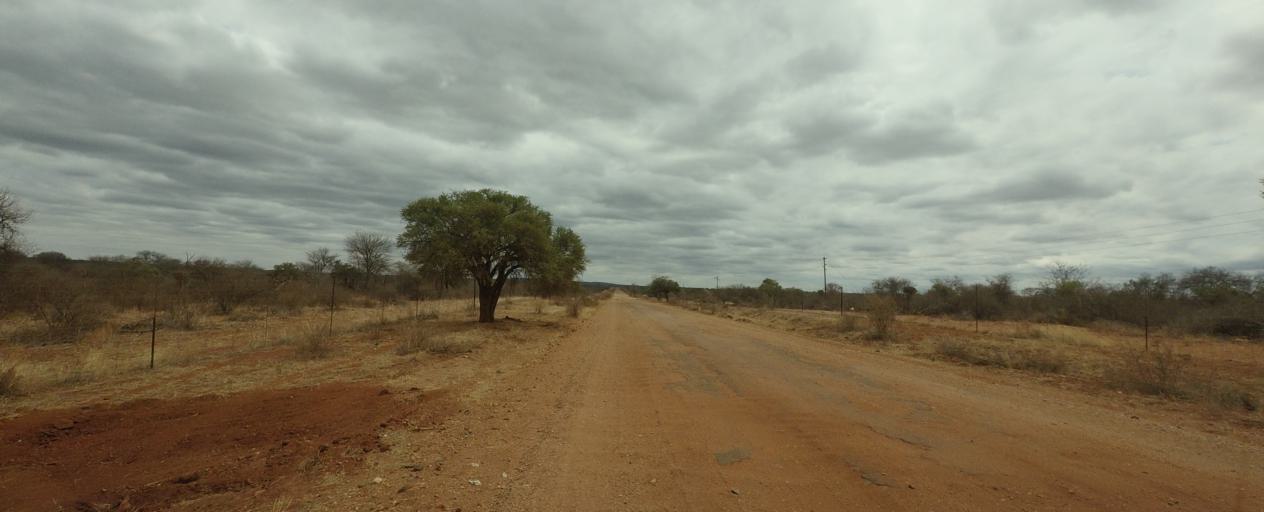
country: BW
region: Central
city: Mathathane
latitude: -22.7398
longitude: 28.4803
